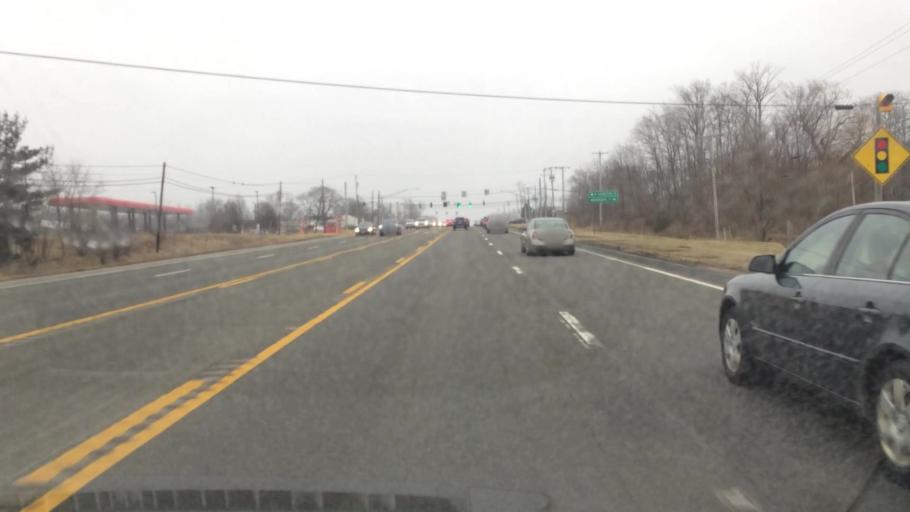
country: US
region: Ohio
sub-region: Summit County
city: Montrose-Ghent
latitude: 41.1363
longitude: -81.7382
